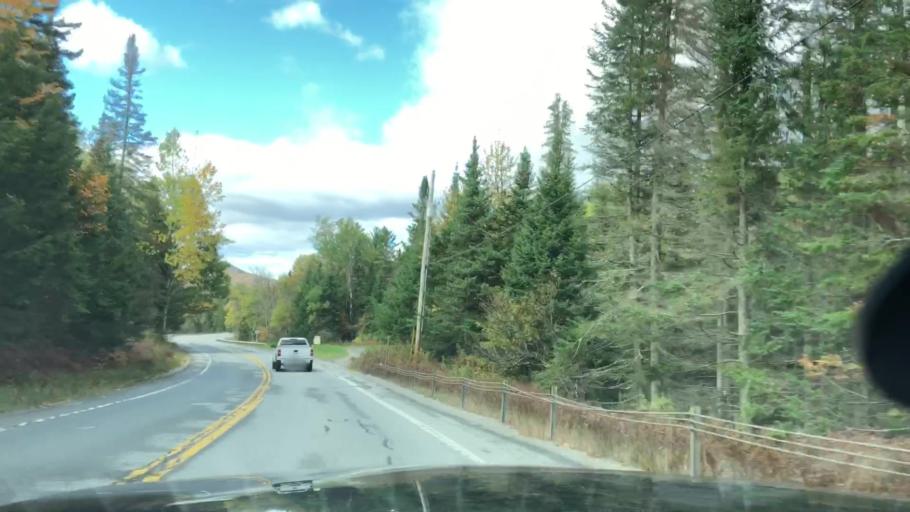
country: US
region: New York
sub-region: Essex County
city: Lake Placid
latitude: 43.8705
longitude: -74.0003
